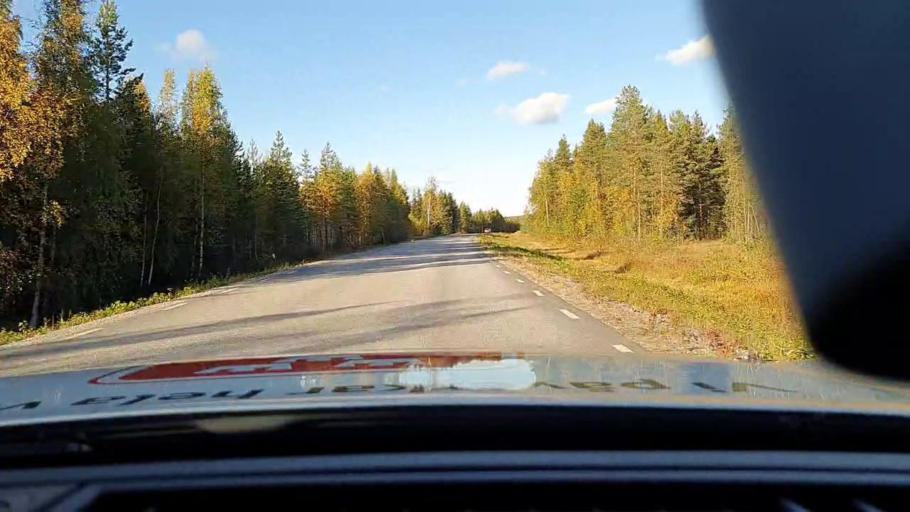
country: SE
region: Norrbotten
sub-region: Pitea Kommun
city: Norrfjarden
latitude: 65.5008
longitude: 21.4761
